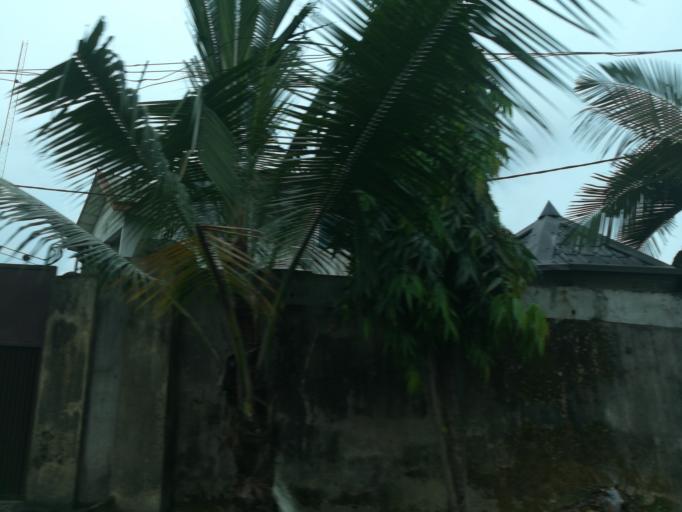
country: NG
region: Rivers
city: Port Harcourt
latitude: 4.8115
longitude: 6.9944
